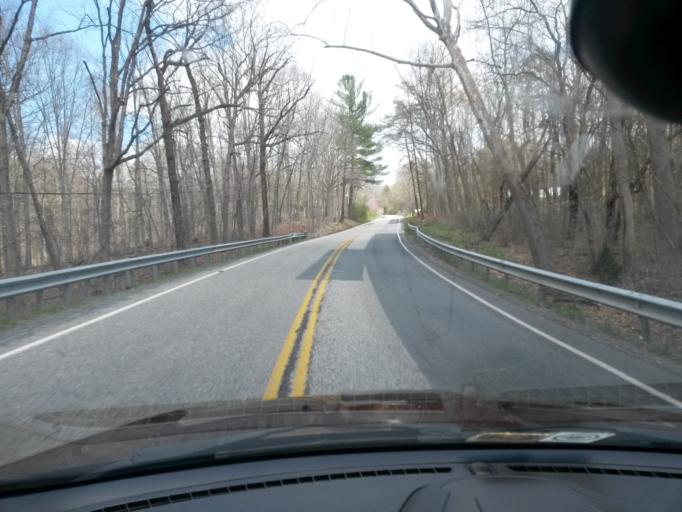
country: US
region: Virginia
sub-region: Rockbridge County
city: Glasgow
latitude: 37.6826
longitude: -79.4060
